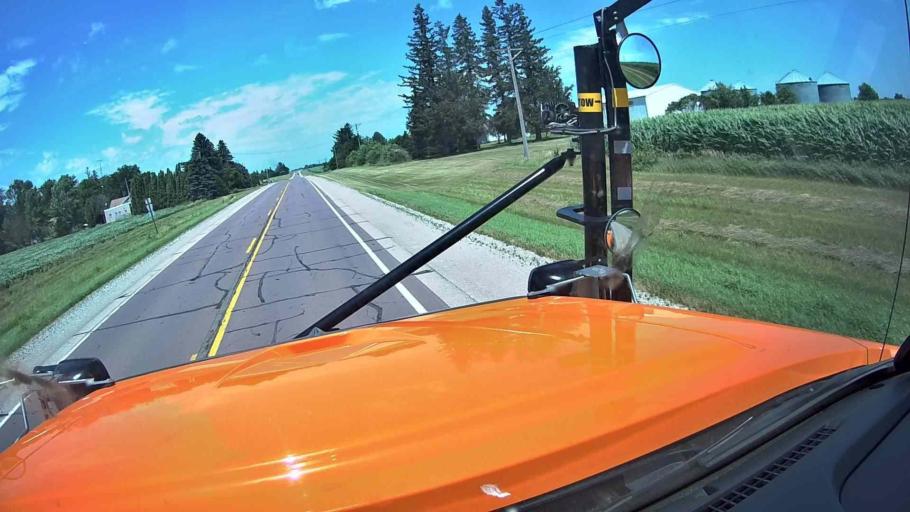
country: US
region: Iowa
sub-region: Cerro Gordo County
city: Mason City
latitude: 43.0692
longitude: -93.2013
